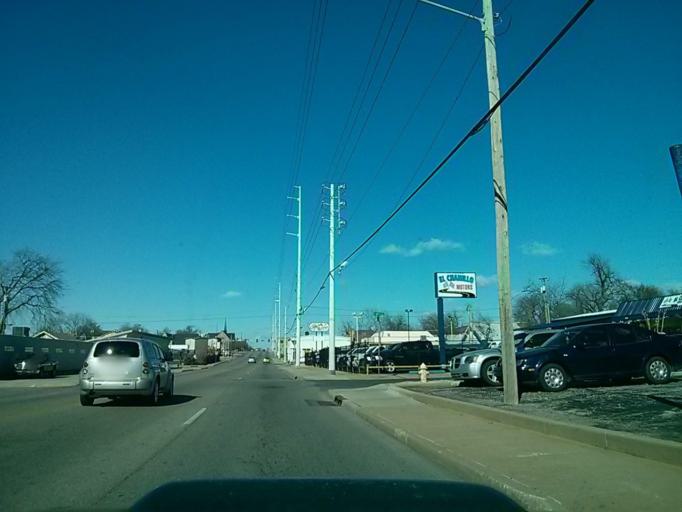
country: US
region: Oklahoma
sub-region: Tulsa County
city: Tulsa
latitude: 36.1496
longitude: -95.9581
